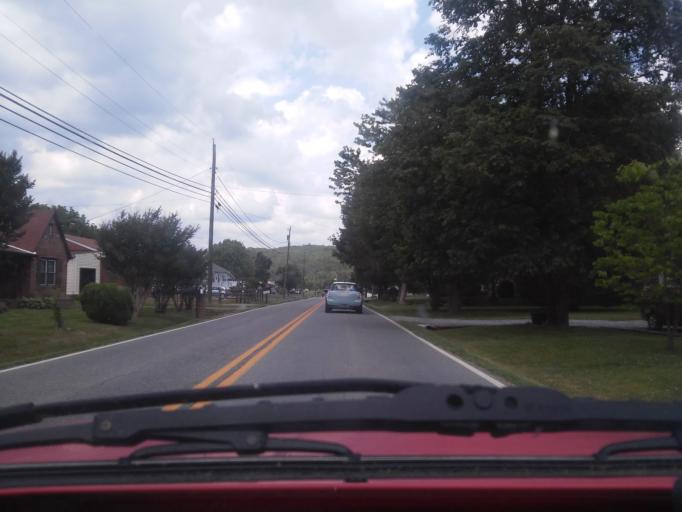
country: US
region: Virginia
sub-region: Craig County
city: New Castle
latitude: 37.5086
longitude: -80.1037
